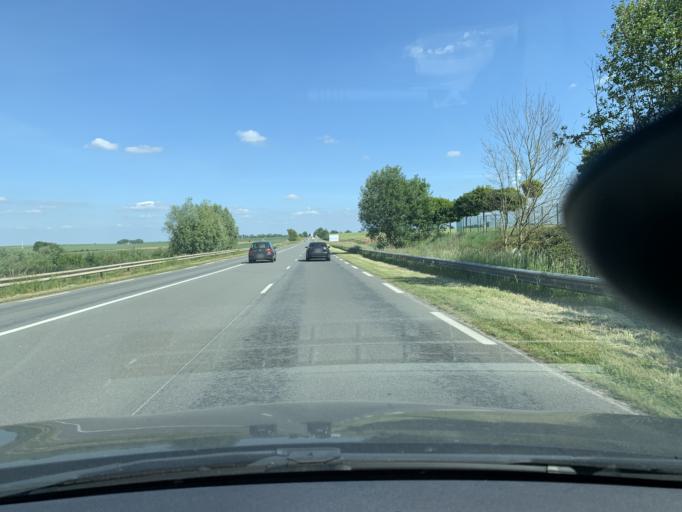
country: FR
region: Nord-Pas-de-Calais
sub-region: Departement du Nord
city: Caudry
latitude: 50.1297
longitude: 3.4306
